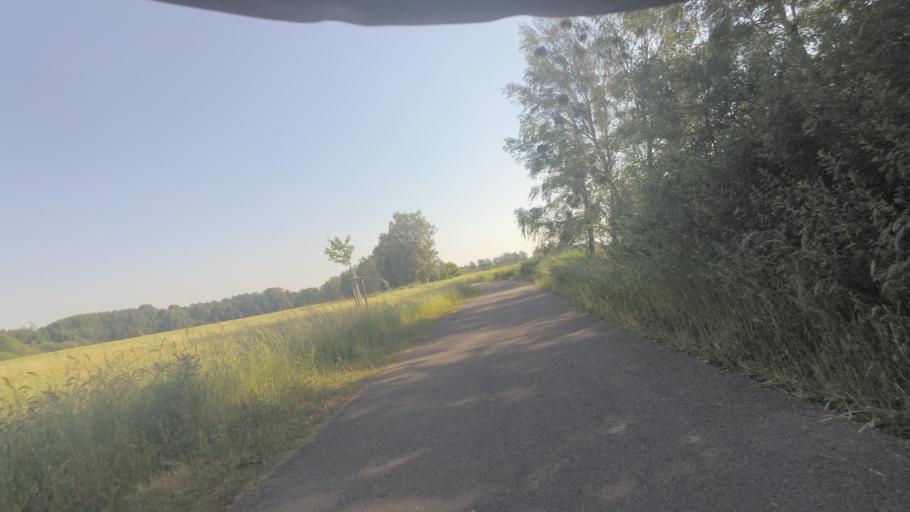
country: DE
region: Saxony-Anhalt
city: Rodleben
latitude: 51.8313
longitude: 12.1655
